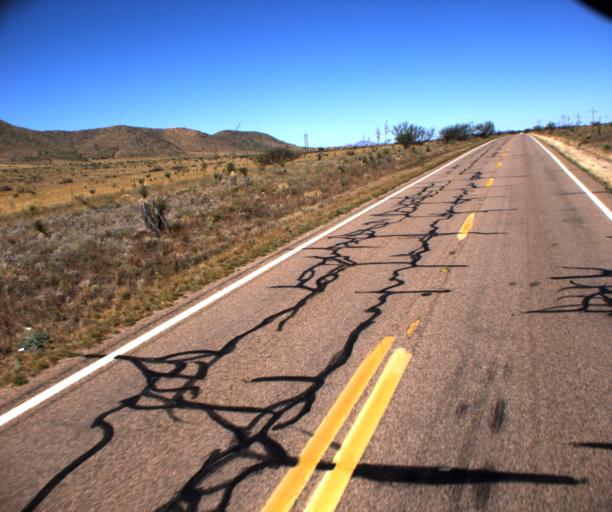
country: US
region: Arizona
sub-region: Cochise County
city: Huachuca City
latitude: 31.7180
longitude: -110.4724
